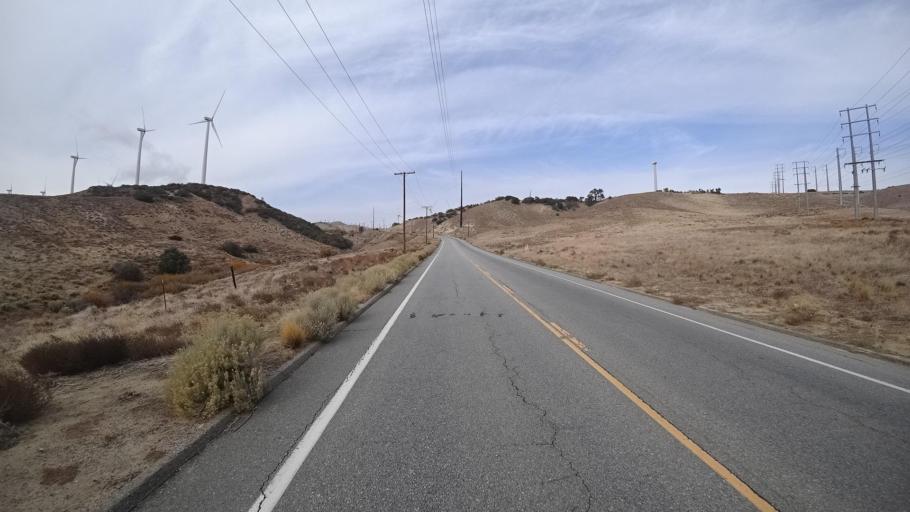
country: US
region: California
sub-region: Kern County
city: Tehachapi
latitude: 35.0541
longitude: -118.3648
